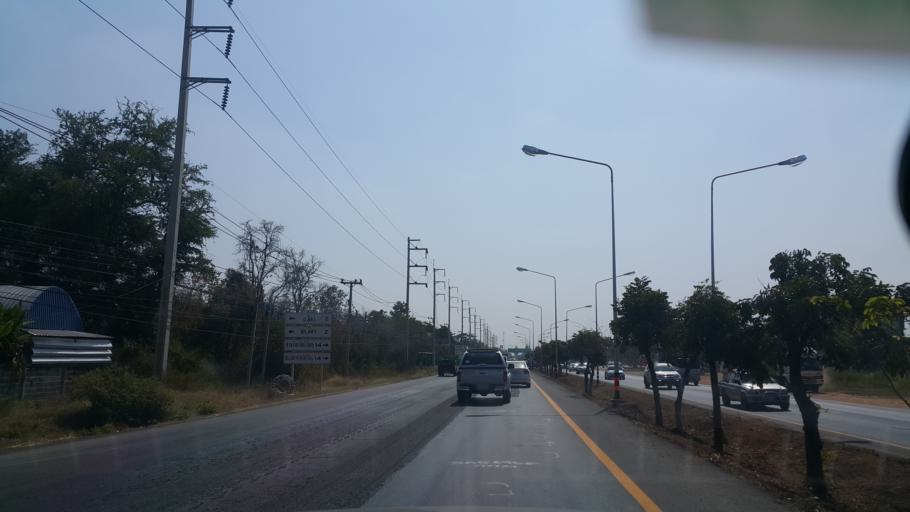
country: TH
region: Nakhon Ratchasima
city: Sida
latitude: 15.5529
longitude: 102.5495
